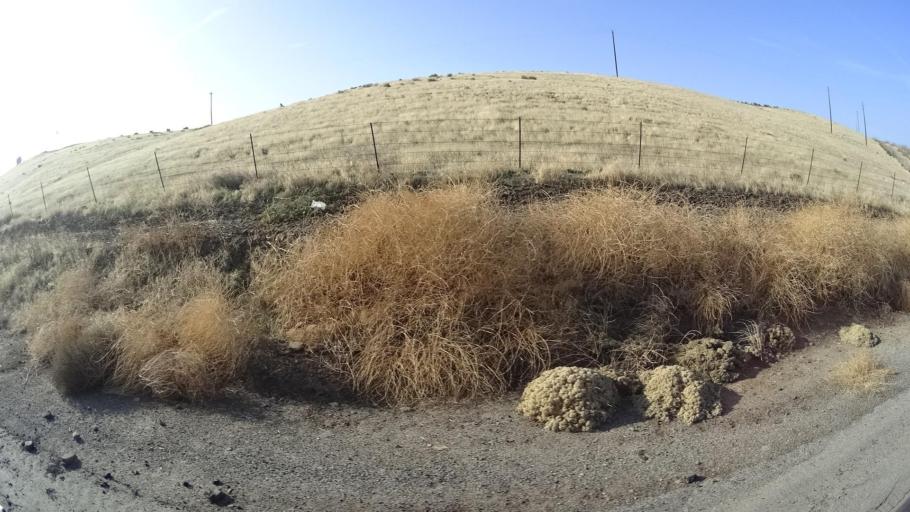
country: US
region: California
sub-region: Tulare County
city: Richgrove
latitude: 35.6460
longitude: -119.0555
